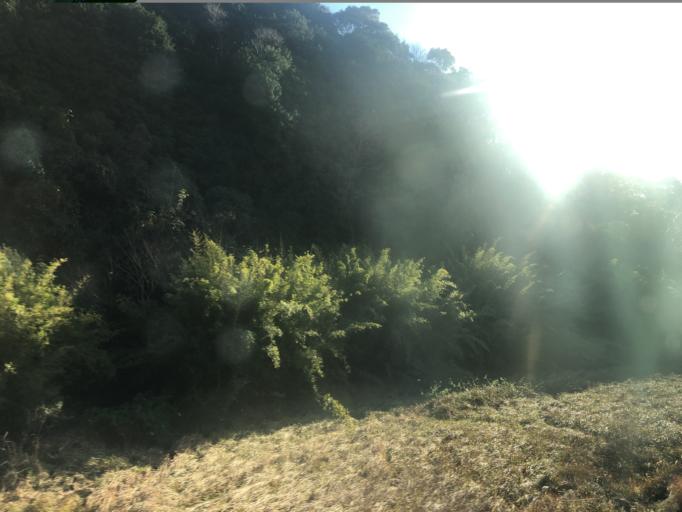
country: JP
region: Kochi
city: Nakamura
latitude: 33.0095
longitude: 132.9884
